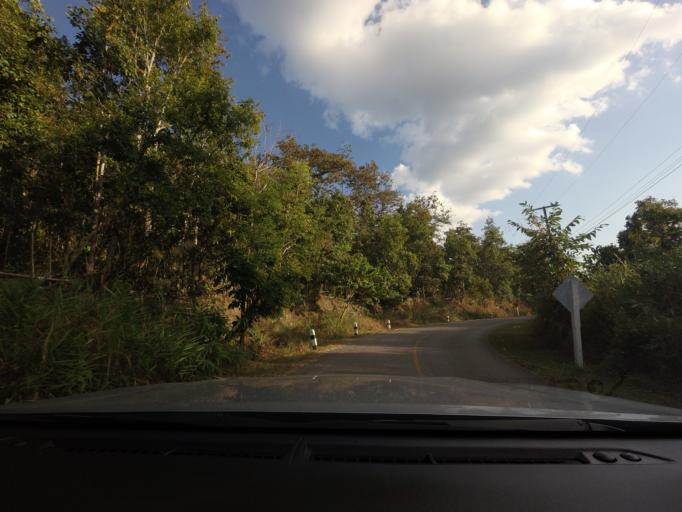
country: TH
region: Chiang Mai
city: Phrao
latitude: 19.5046
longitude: 99.1690
